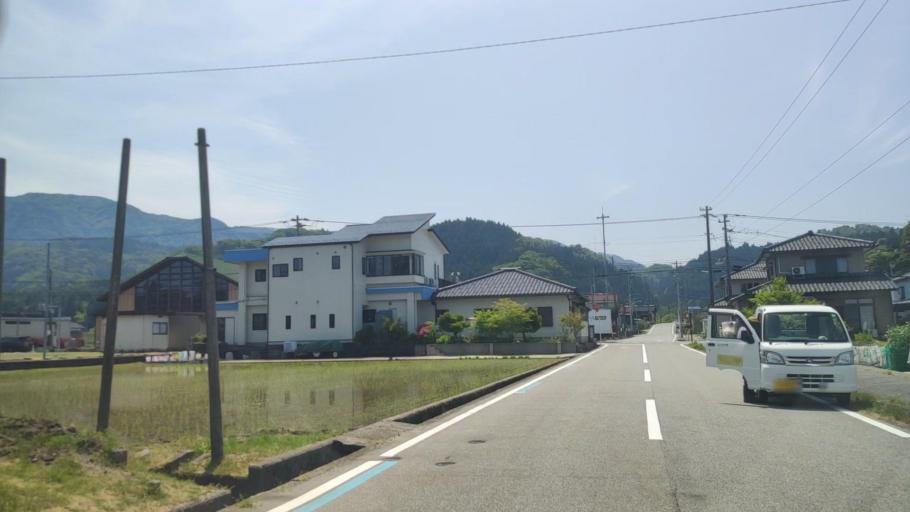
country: JP
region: Toyama
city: Nyuzen
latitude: 36.9740
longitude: 137.5922
